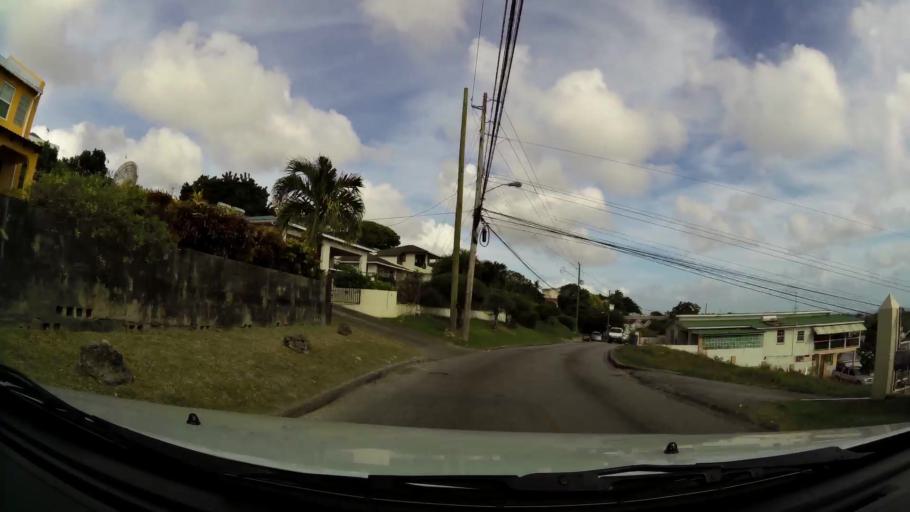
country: BB
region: Saint Michael
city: Bridgetown
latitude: 13.0869
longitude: -59.5861
